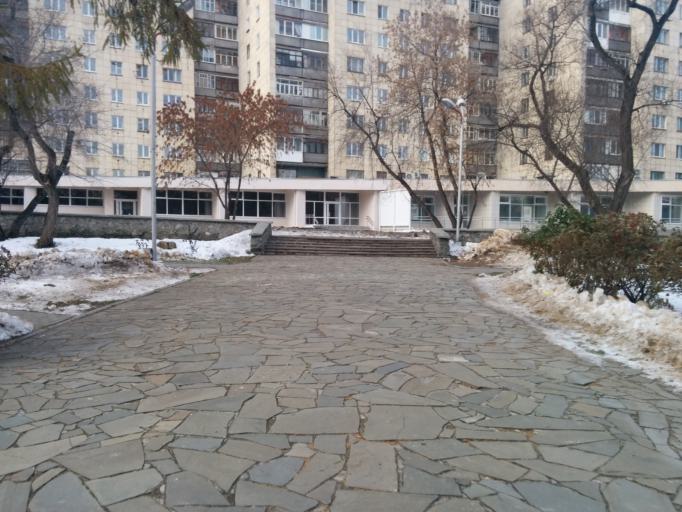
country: RU
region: Perm
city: Perm
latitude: 58.0130
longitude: 56.2316
